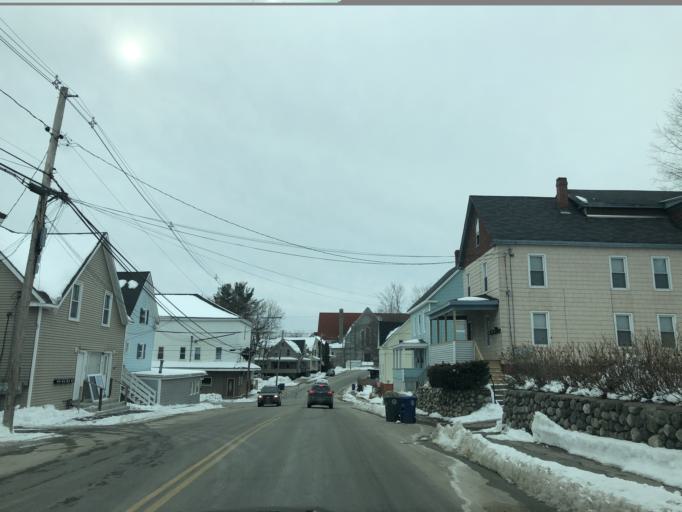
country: US
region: Maine
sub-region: Cumberland County
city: Westbrook
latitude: 43.6808
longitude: -70.3617
